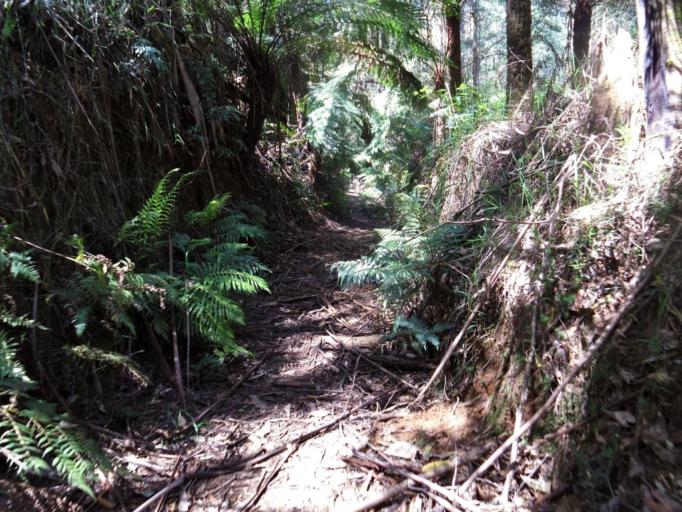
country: AU
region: Victoria
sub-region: Yarra Ranges
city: Millgrove
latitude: -37.8598
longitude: 145.7626
